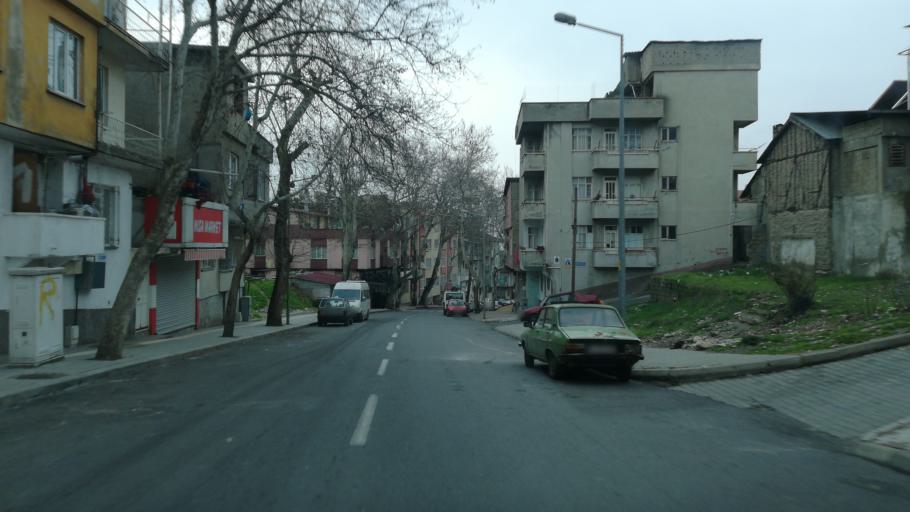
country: TR
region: Kahramanmaras
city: Kahramanmaras
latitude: 37.5915
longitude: 36.9270
